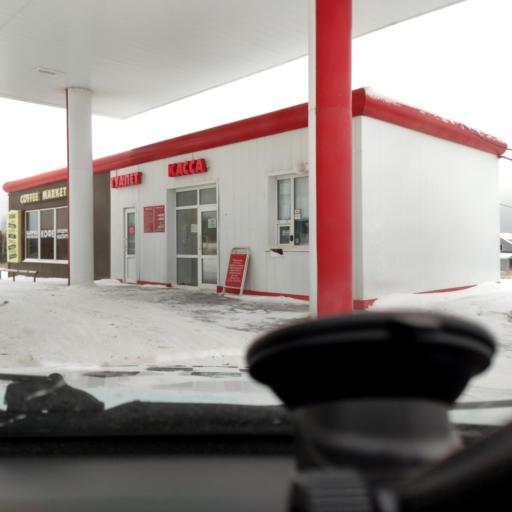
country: RU
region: Perm
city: Yugo-Kamskiy
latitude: 57.6933
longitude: 55.5869
